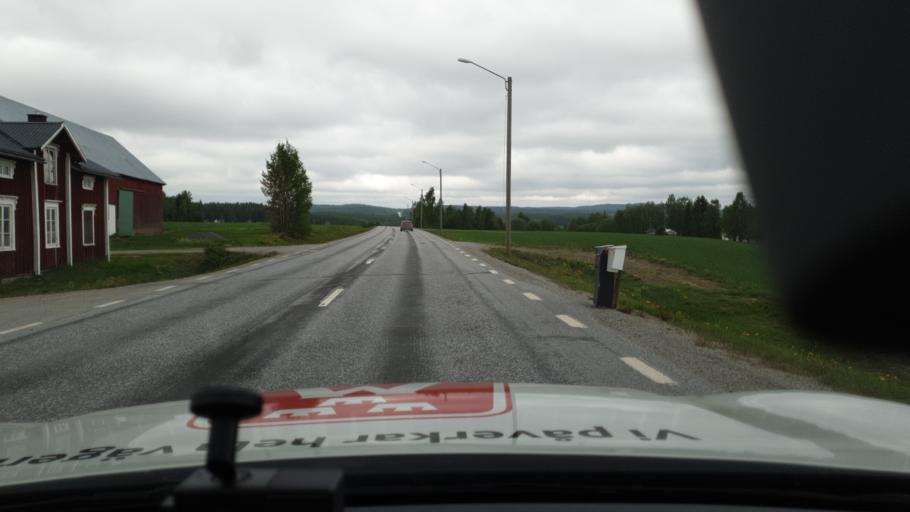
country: SE
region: Vaesterbotten
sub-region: Vannas Kommun
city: Vannasby
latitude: 64.0166
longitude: 20.0307
